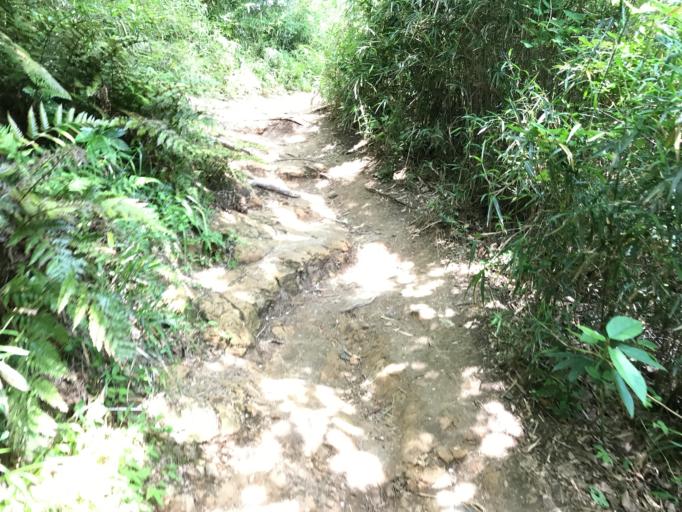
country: JP
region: Kanagawa
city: Kamakura
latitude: 35.3202
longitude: 139.5346
